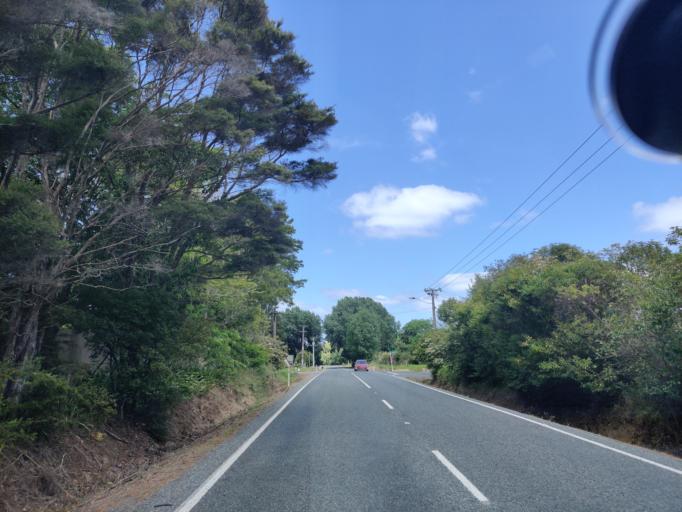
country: NZ
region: Auckland
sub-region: Auckland
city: Parakai
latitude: -36.6129
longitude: 174.4895
